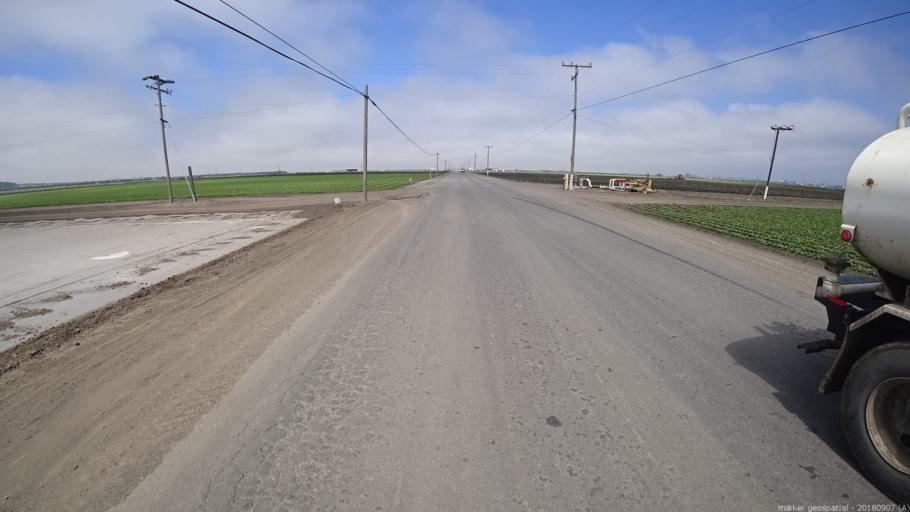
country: US
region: California
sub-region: Monterey County
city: Castroville
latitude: 36.7252
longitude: -121.7479
